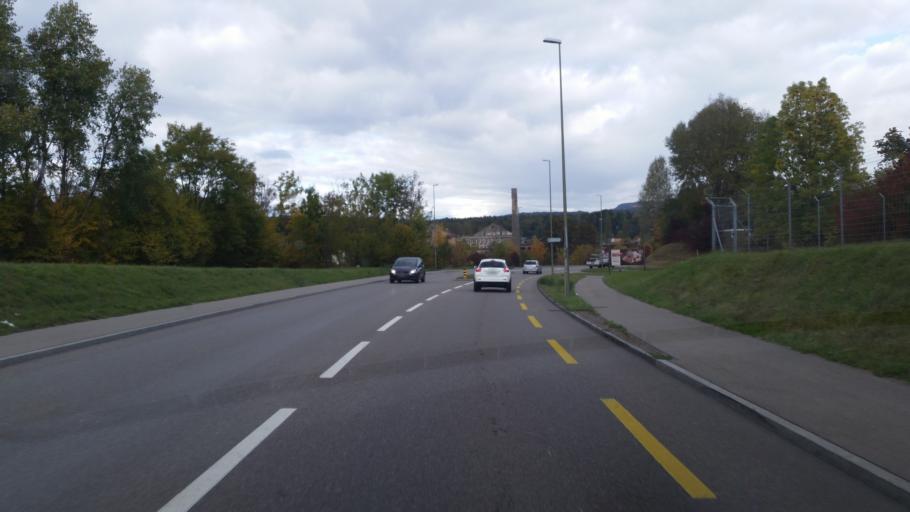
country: CH
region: Zurich
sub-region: Bezirk Buelach
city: Hochfelden
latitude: 47.5136
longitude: 8.5210
